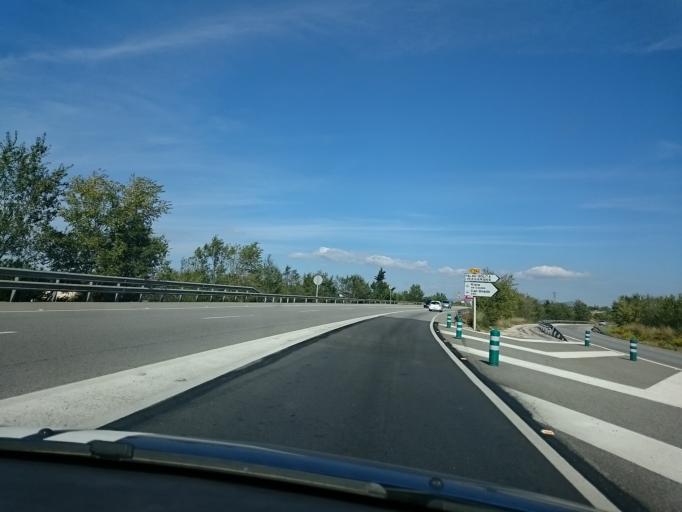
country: ES
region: Catalonia
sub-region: Provincia de Barcelona
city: Santa Perpetua de Mogoda
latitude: 41.5566
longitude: 2.1851
